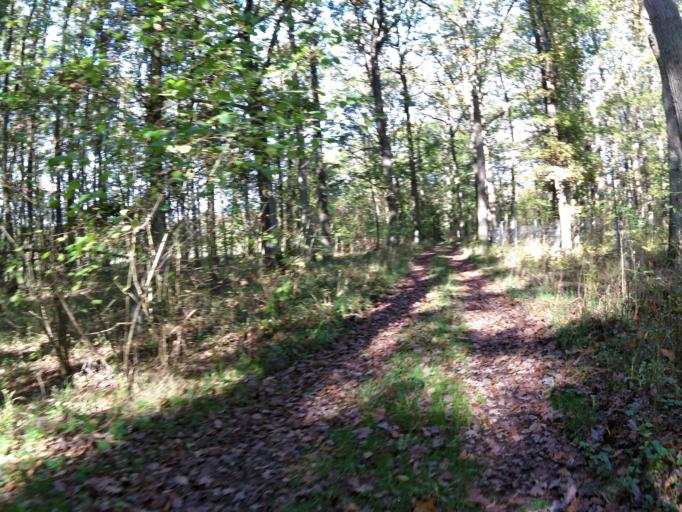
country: DE
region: Bavaria
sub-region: Regierungsbezirk Unterfranken
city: Sulzfeld am Main
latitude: 49.7151
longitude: 10.0979
